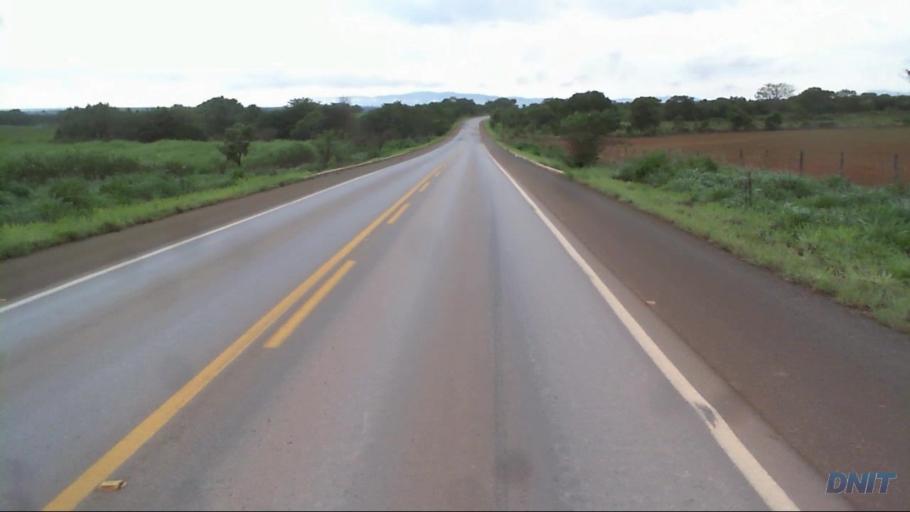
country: BR
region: Goias
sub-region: Uruacu
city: Uruacu
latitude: -14.7239
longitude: -49.0975
